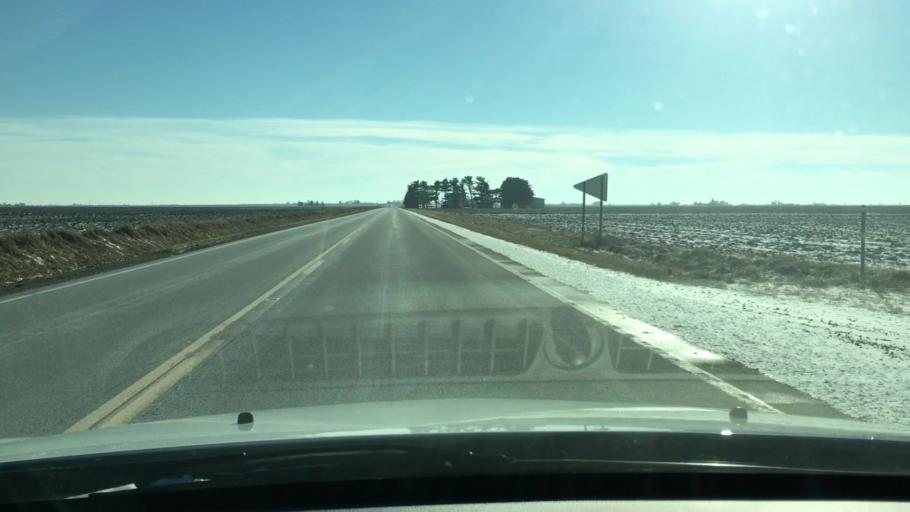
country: US
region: Illinois
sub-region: Ogle County
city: Rochelle
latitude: 41.8700
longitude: -89.0731
